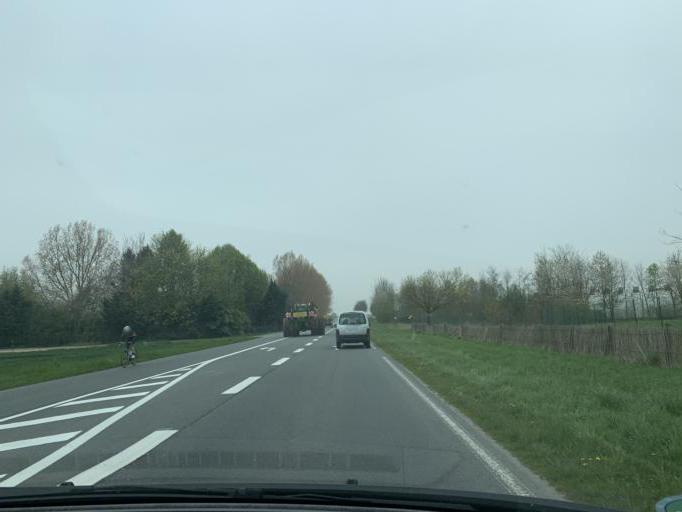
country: FR
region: Picardie
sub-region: Departement de la Somme
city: Abbeville
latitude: 50.1403
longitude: 1.8244
